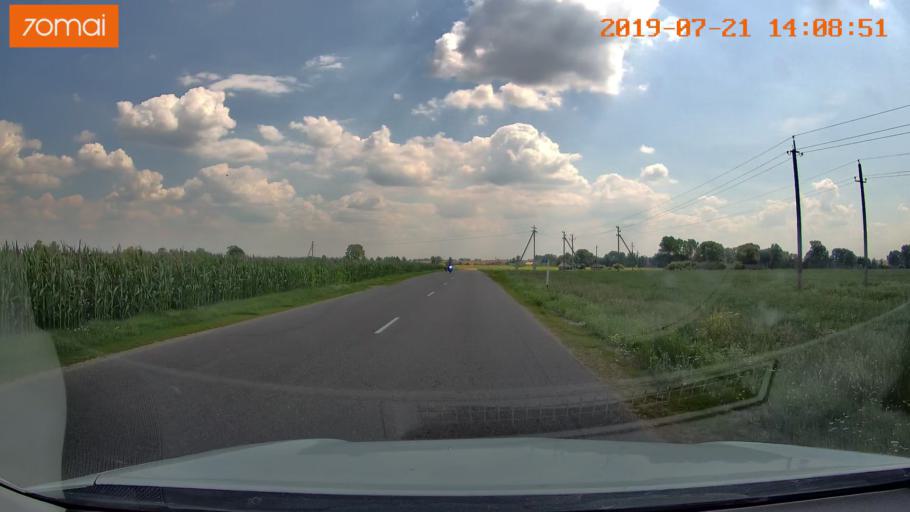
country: BY
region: Grodnenskaya
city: Karelichy
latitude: 53.6701
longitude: 26.1295
